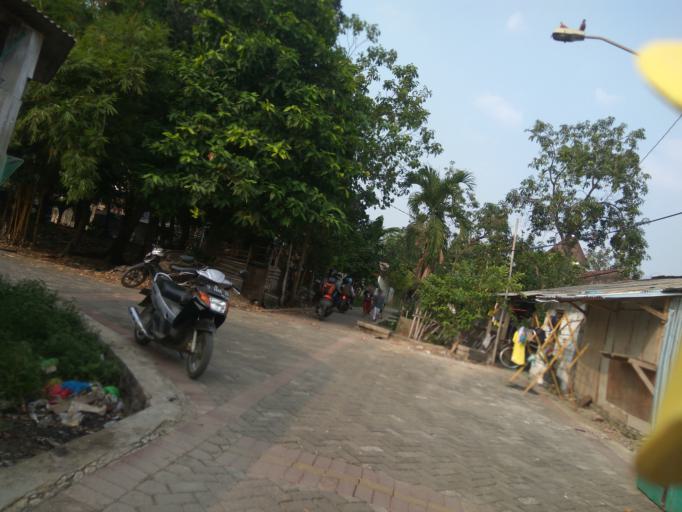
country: ID
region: Central Java
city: Semarang
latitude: -6.9703
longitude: 110.3955
